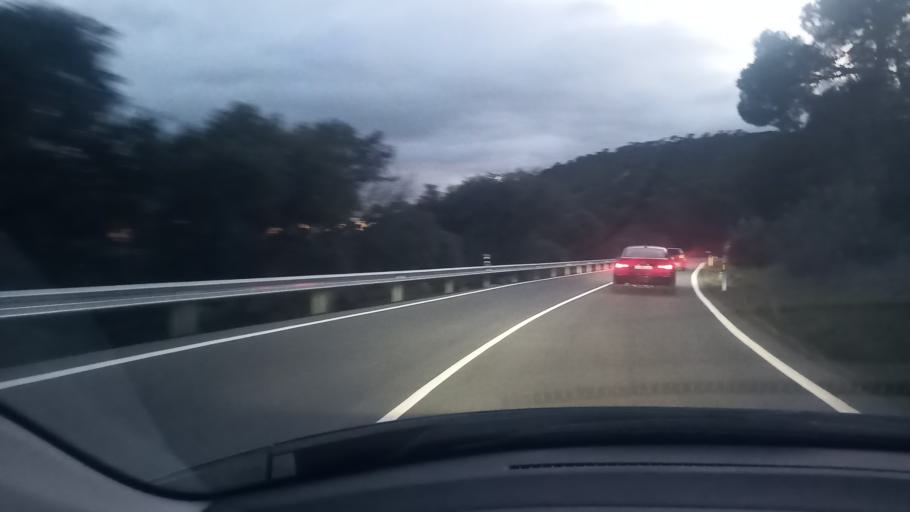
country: ES
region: Madrid
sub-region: Provincia de Madrid
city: Navas del Rey
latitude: 40.4431
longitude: -4.2658
